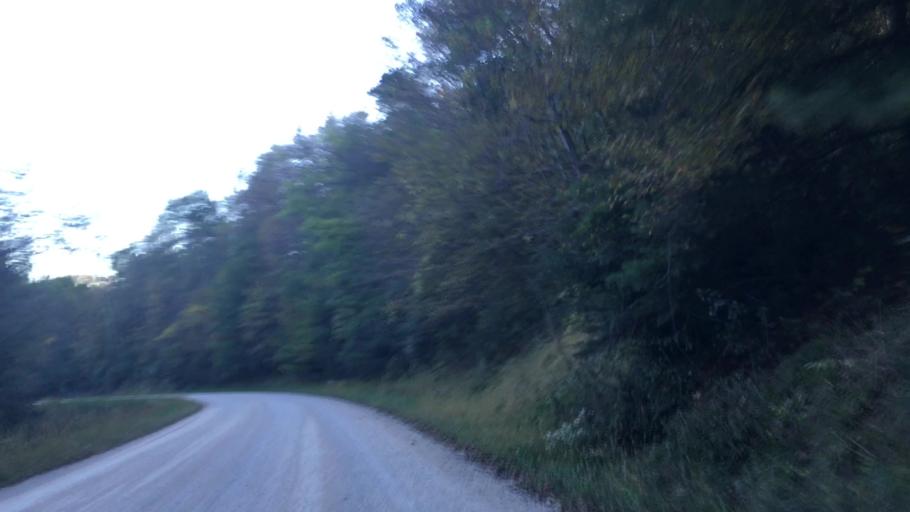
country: US
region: Minnesota
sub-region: Fillmore County
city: Preston
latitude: 43.7832
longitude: -92.0385
